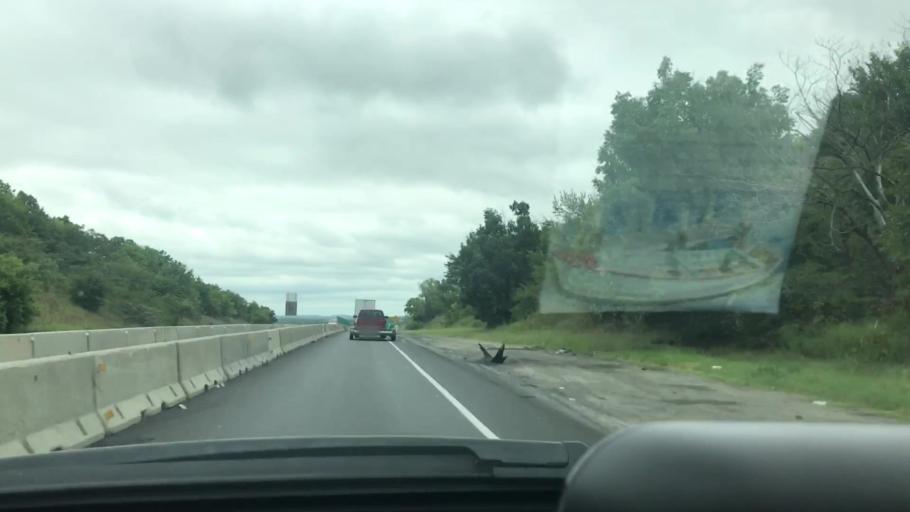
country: US
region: Oklahoma
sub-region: McIntosh County
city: Eufaula
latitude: 35.2887
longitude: -95.5931
